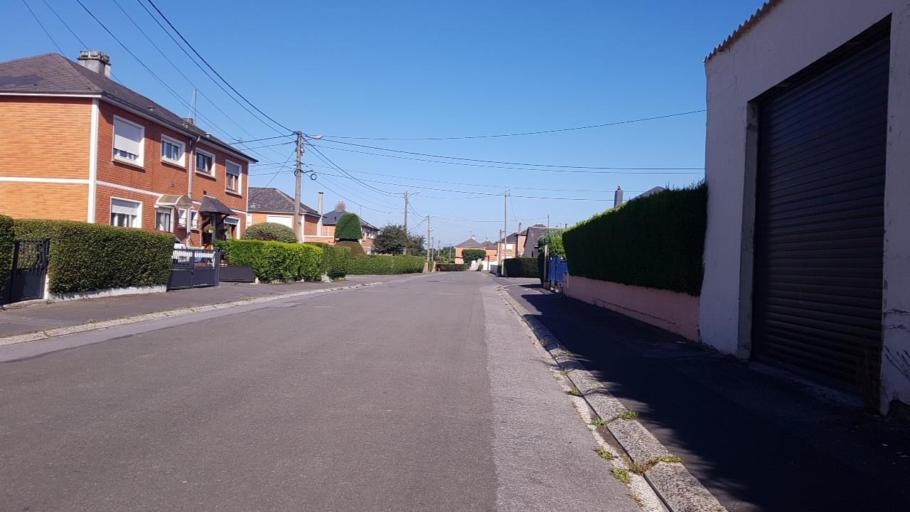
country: FR
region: Picardie
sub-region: Departement de l'Aisne
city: Hirson
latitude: 49.9264
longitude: 4.0739
